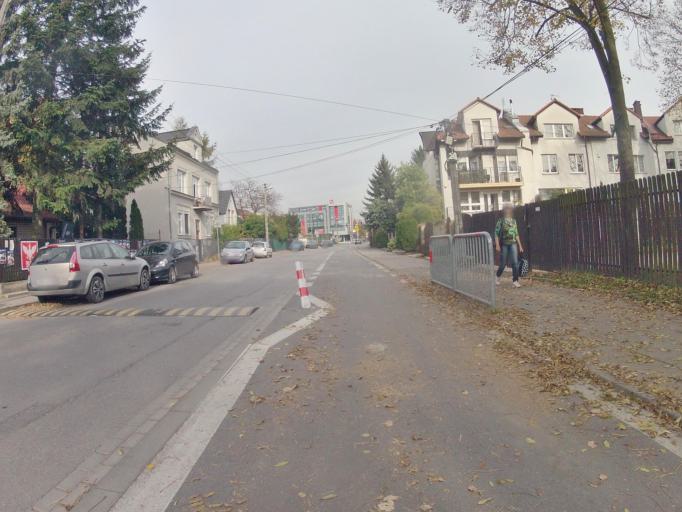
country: PL
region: Lesser Poland Voivodeship
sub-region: Krakow
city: Krakow
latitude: 50.0427
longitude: 19.9211
